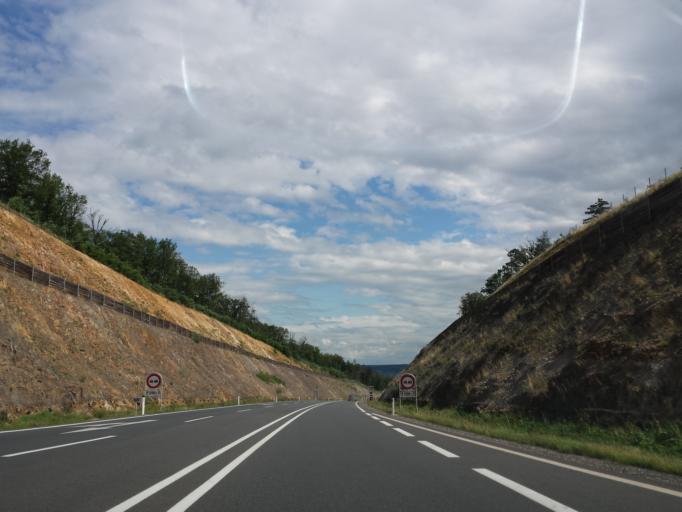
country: AT
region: Lower Austria
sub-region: Politischer Bezirk Hollabrunn
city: Maissau
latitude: 48.5824
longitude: 15.8312
